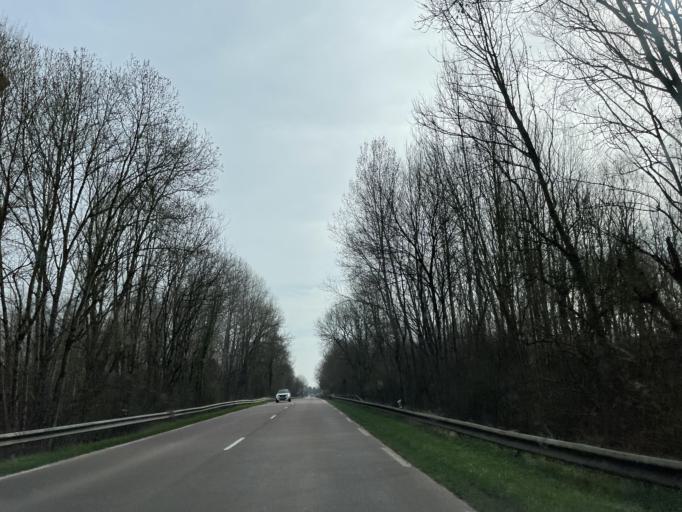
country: FR
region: Champagne-Ardenne
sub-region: Departement de l'Aube
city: Nogent-sur-Seine
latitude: 48.5040
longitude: 3.4527
